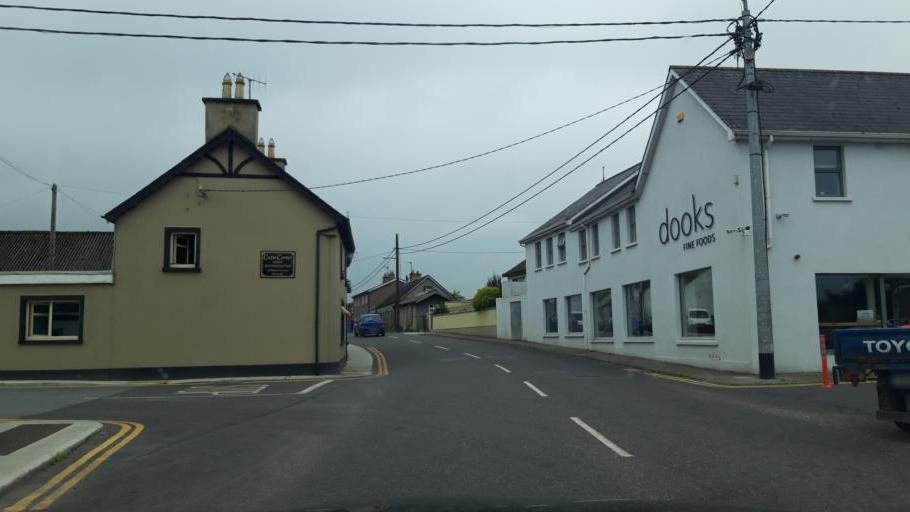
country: IE
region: Munster
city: Fethard
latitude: 52.4655
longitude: -7.6995
